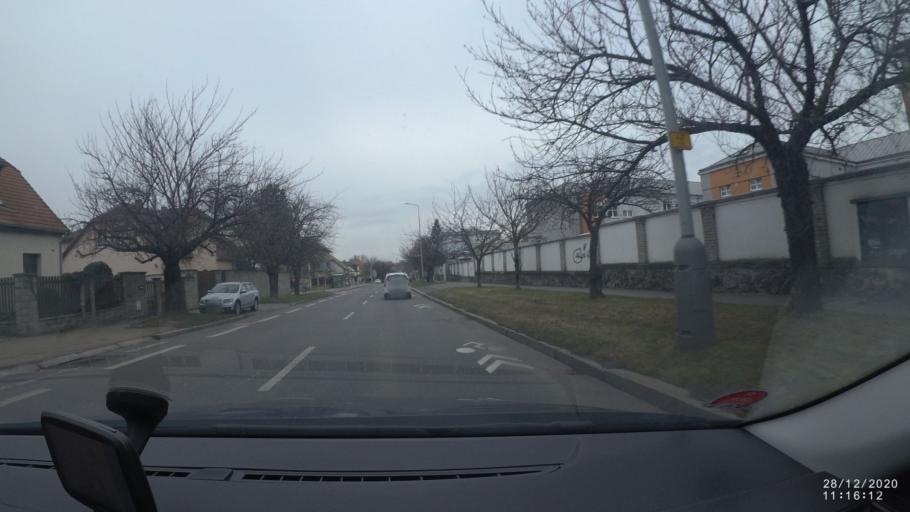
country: CZ
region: Praha
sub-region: Praha 18
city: Letnany
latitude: 50.1341
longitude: 14.5138
